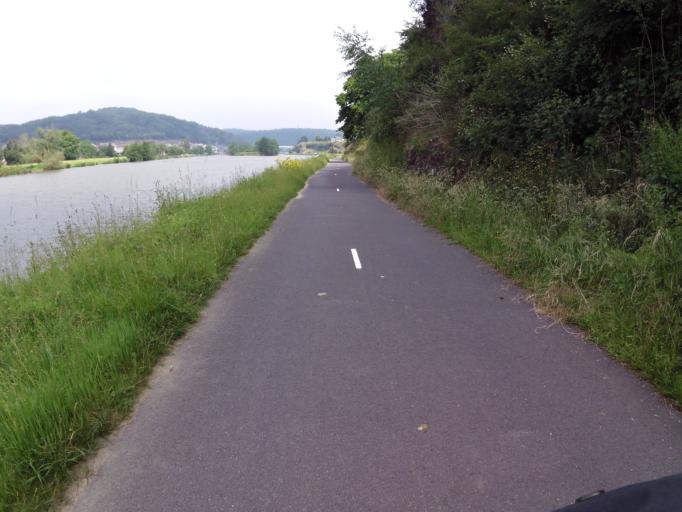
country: FR
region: Champagne-Ardenne
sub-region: Departement des Ardennes
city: Vireux-Molhain
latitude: 50.0761
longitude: 4.7287
